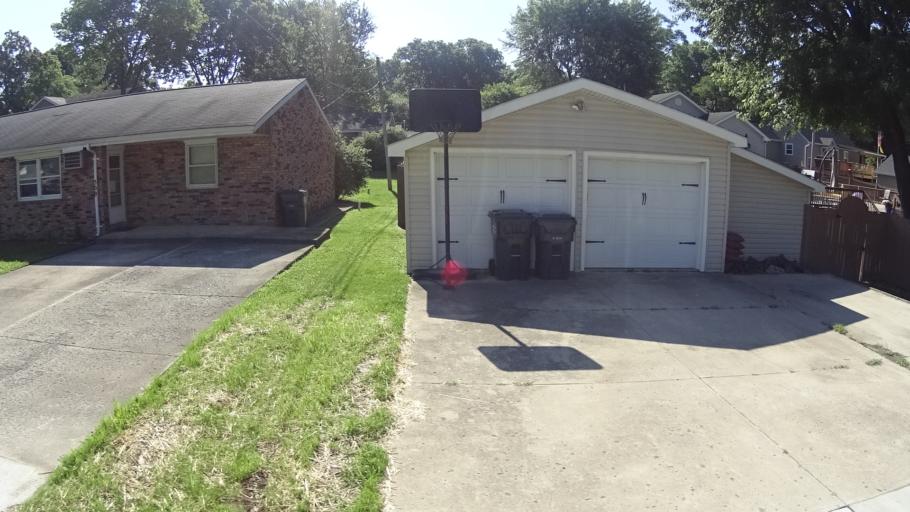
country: US
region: Indiana
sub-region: Madison County
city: Pendleton
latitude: 39.9970
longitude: -85.7475
